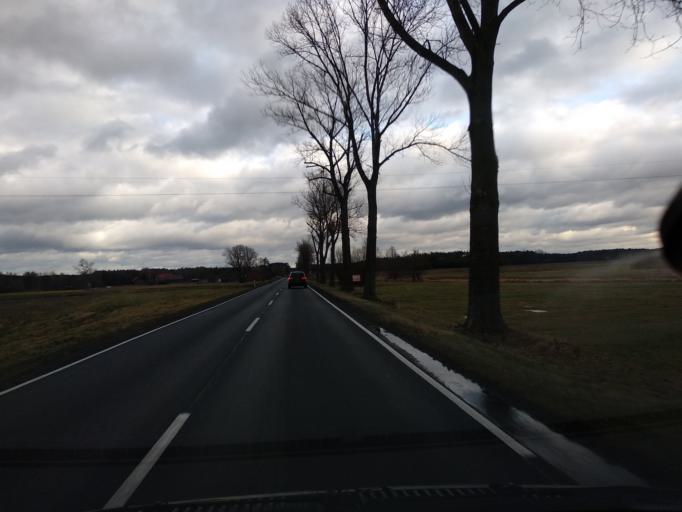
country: PL
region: Greater Poland Voivodeship
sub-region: Powiat ostrowski
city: Jankow Przygodzki
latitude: 51.4901
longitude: 17.7746
